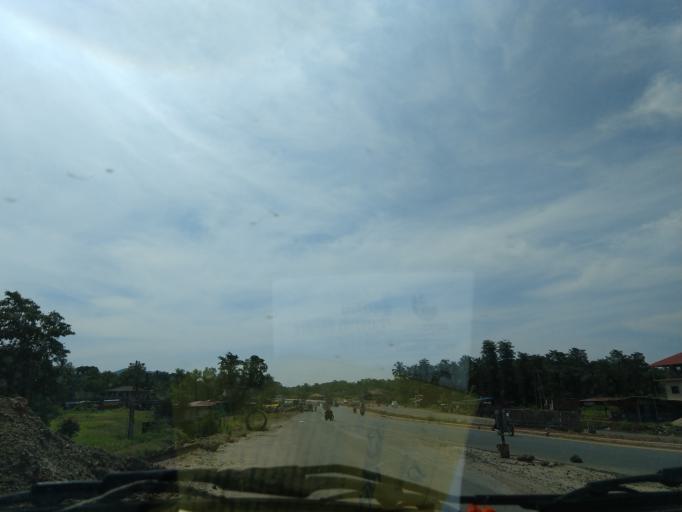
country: IN
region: Maharashtra
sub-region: Sindhudurg
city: Kudal
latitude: 15.9525
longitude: 73.7388
